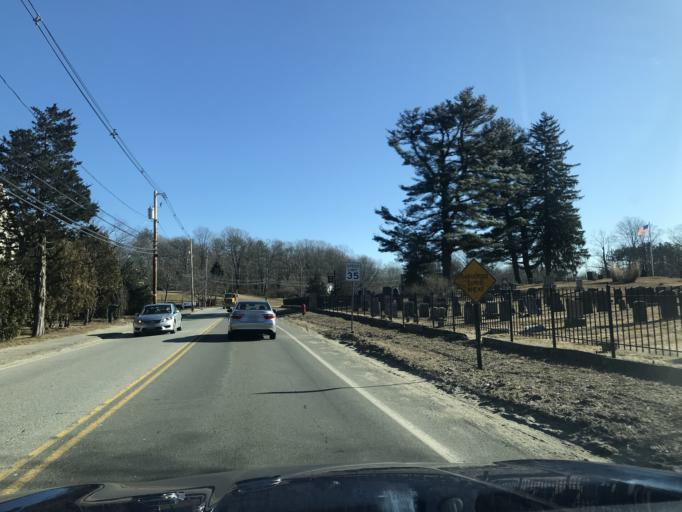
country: US
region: Massachusetts
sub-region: Essex County
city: Boxford
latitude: 42.7195
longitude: -70.9800
